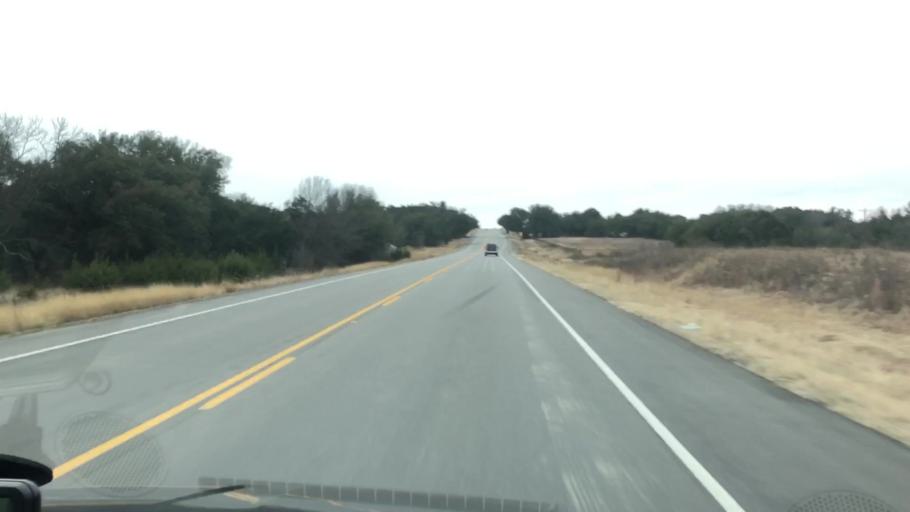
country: US
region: Texas
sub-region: Hamilton County
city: Hico
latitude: 31.9986
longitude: -98.0492
